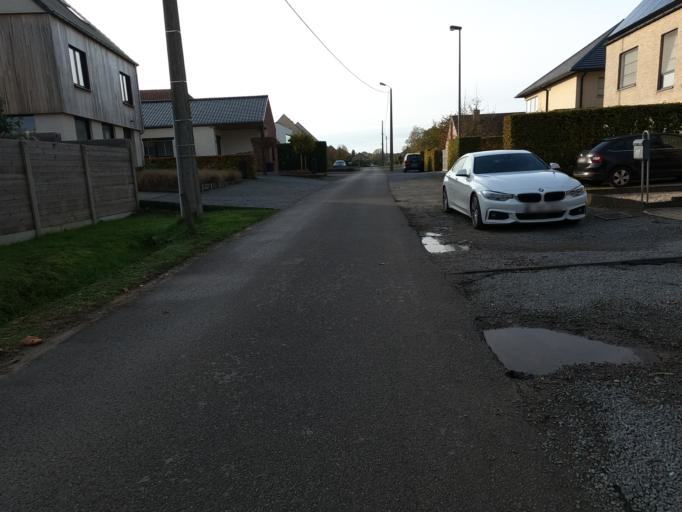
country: BE
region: Flanders
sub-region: Provincie Antwerpen
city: Berlaar
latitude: 51.1438
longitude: 4.6410
